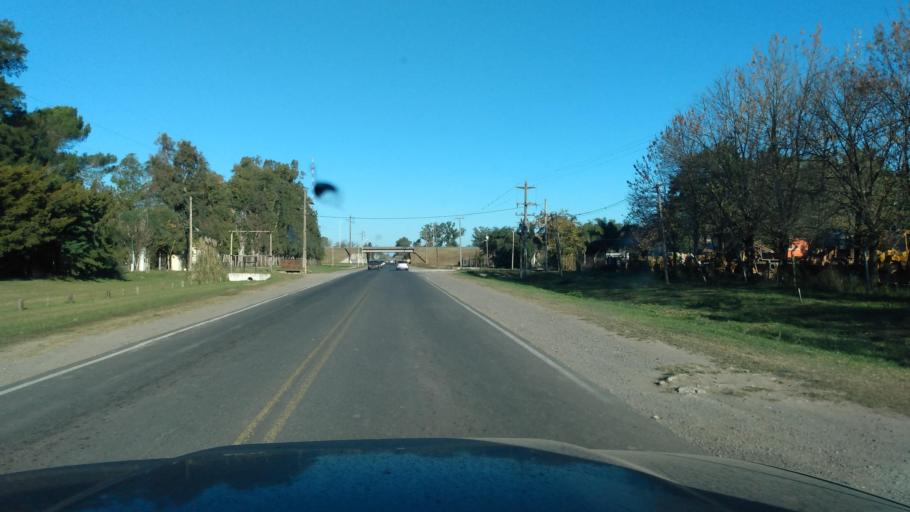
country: AR
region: Buenos Aires
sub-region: Partido de Lujan
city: Lujan
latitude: -34.5421
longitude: -59.1590
